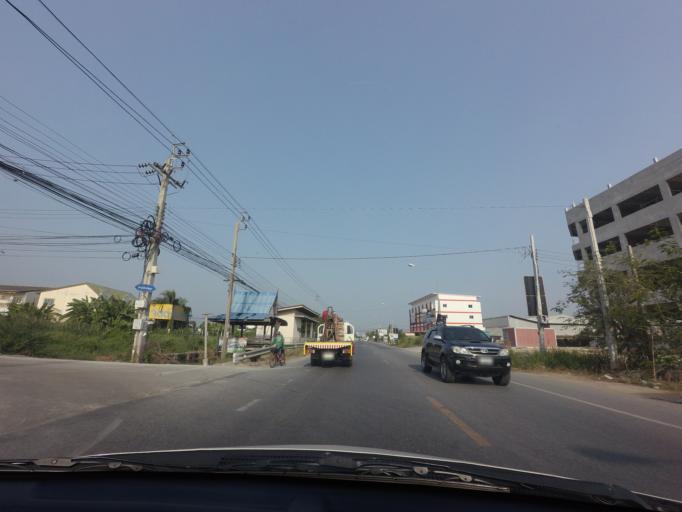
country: TH
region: Nakhon Pathom
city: Salaya
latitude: 13.8115
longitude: 100.3432
